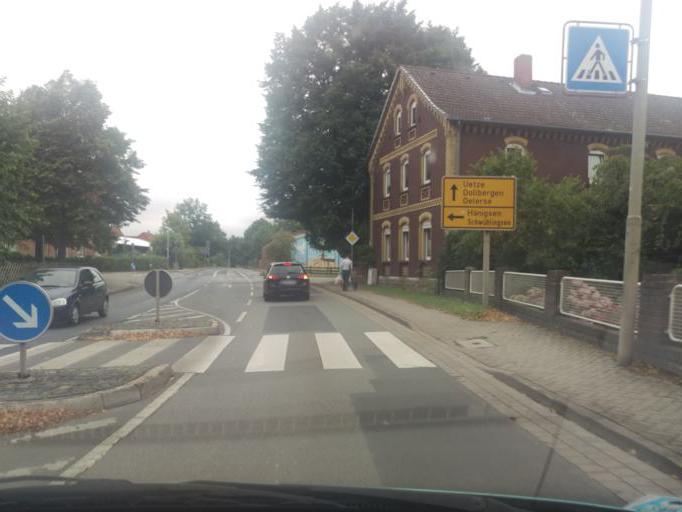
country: DE
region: Lower Saxony
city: Arpke
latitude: 52.3737
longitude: 10.1311
